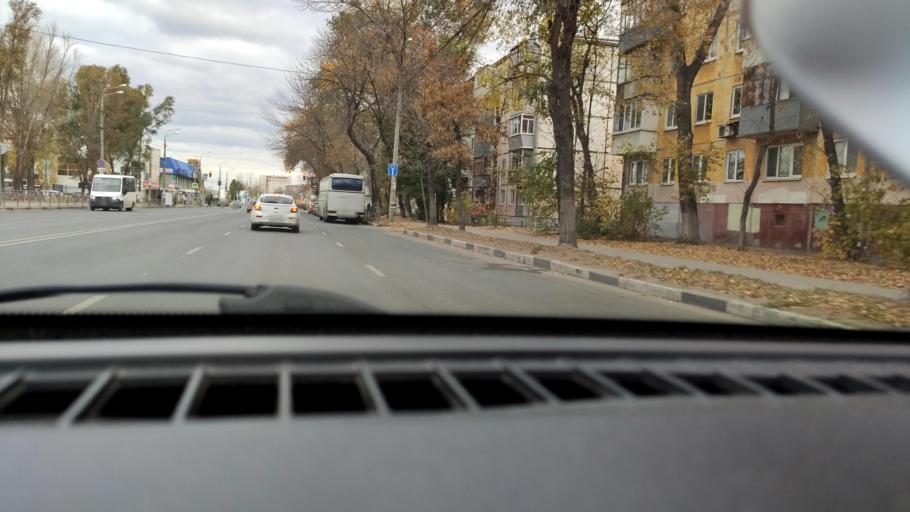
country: RU
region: Samara
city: Samara
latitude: 53.2088
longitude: 50.1896
